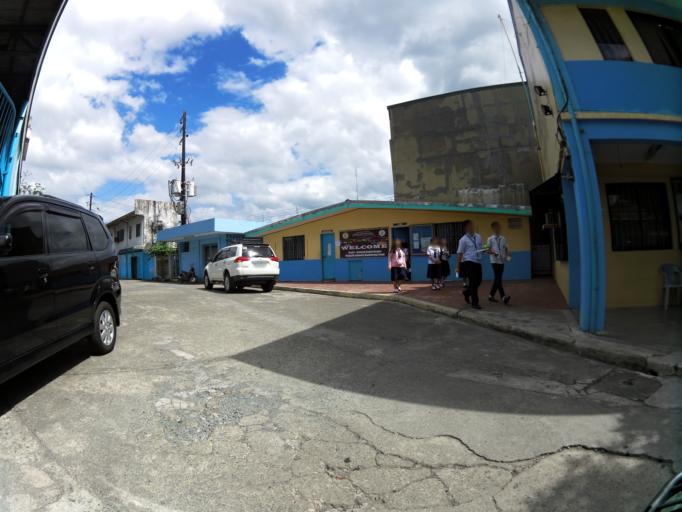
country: PH
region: Metro Manila
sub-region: Marikina
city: Calumpang
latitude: 14.6320
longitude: 121.0993
